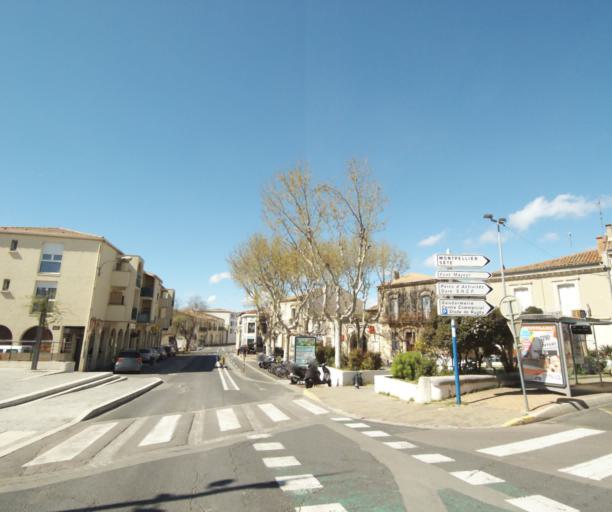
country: FR
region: Languedoc-Roussillon
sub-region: Departement de l'Herault
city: Villeneuve-les-Maguelone
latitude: 43.5332
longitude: 3.8617
